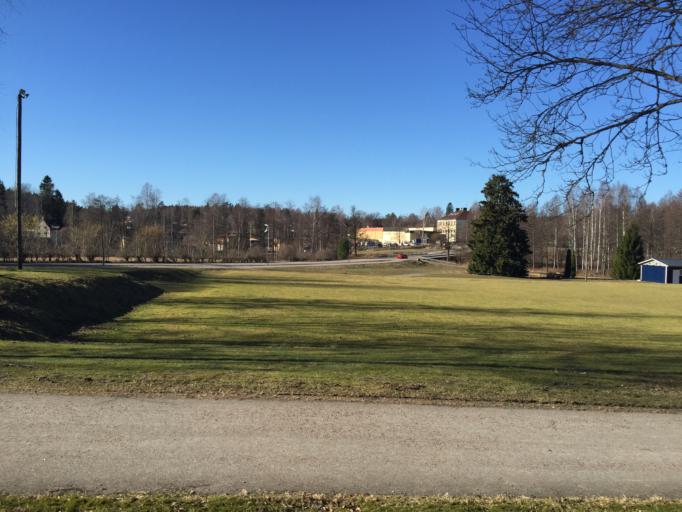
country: SE
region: OEstergoetland
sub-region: Finspangs Kommun
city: Finspang
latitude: 58.7338
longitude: 15.8266
